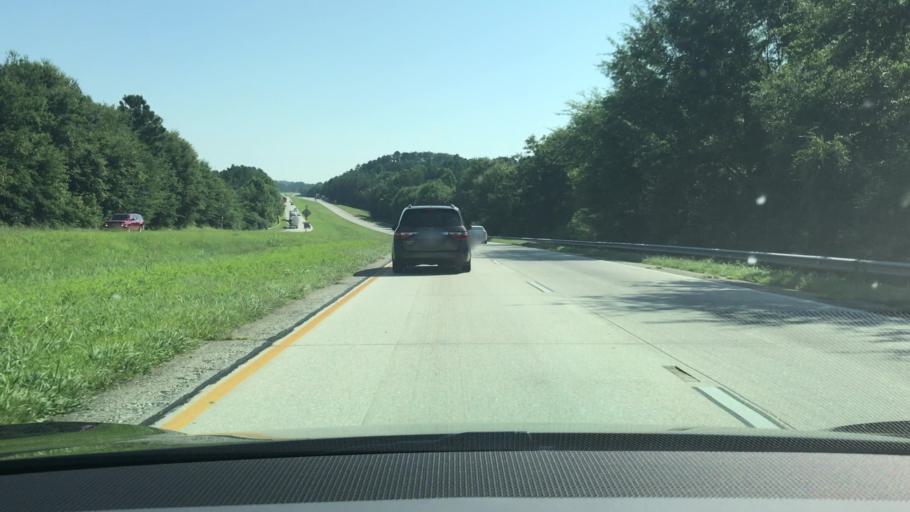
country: US
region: Georgia
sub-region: Hall County
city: Gainesville
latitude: 34.3504
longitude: -83.7573
